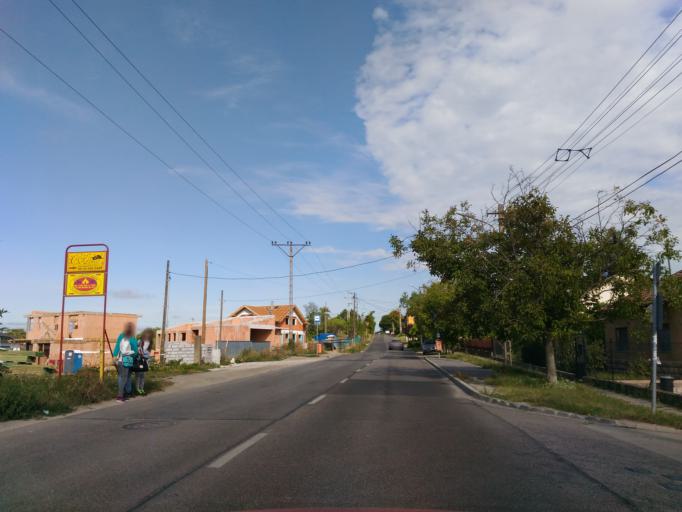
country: HU
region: Pest
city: Diosd
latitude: 47.4110
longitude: 18.9941
